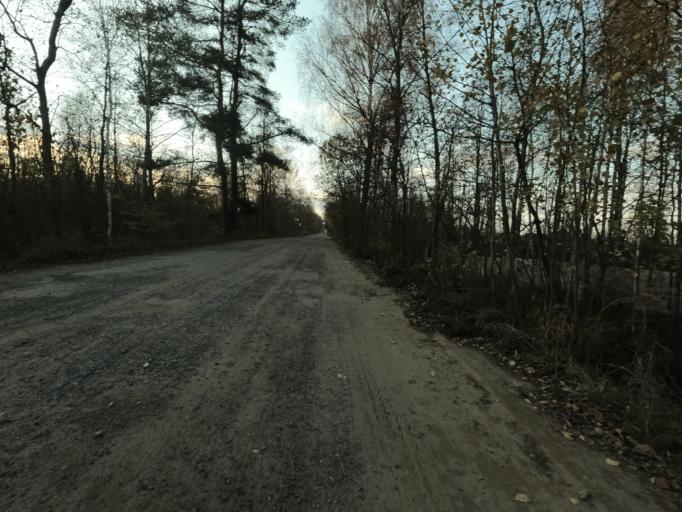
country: RU
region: Leningrad
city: Mga
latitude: 59.7630
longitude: 31.2532
